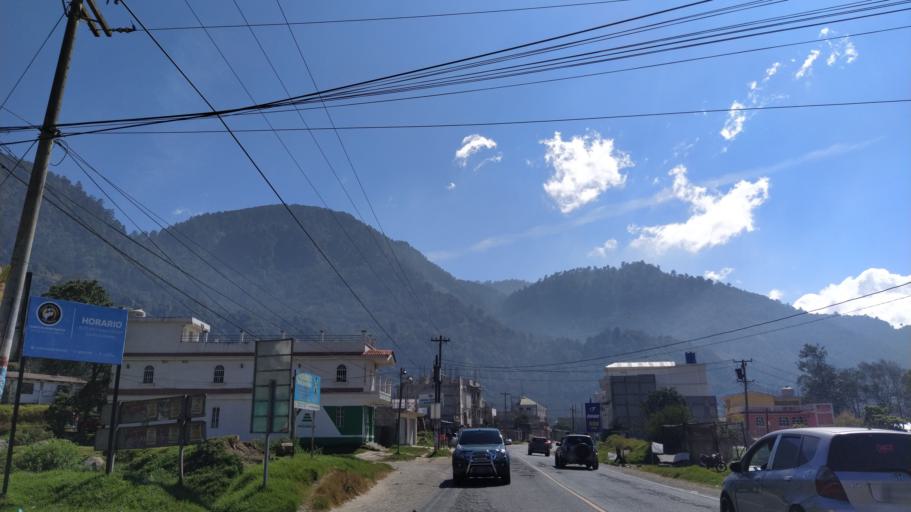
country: GT
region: Quetzaltenango
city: Cantel
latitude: 14.8090
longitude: -91.4477
